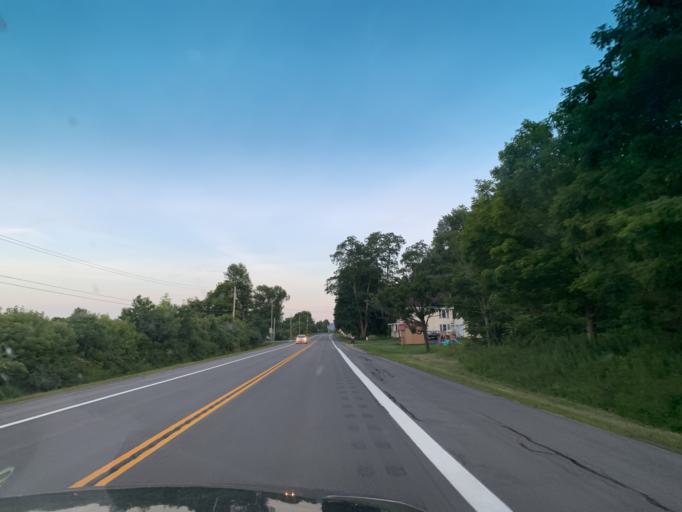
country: US
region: New York
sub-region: Oneida County
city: Chadwicks
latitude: 42.9342
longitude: -75.2503
